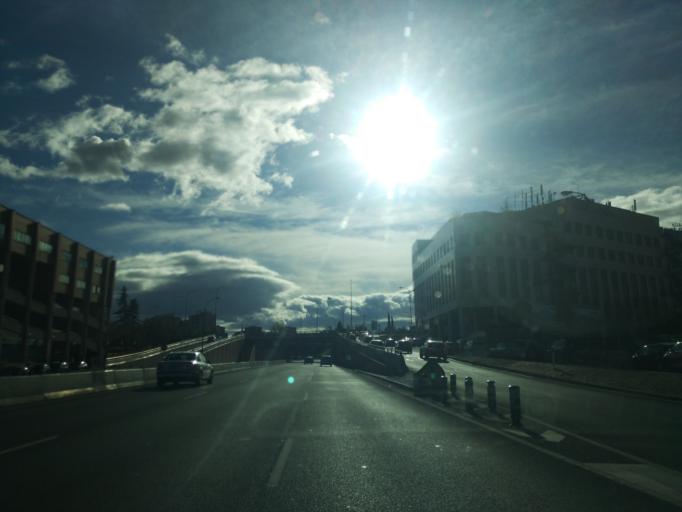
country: ES
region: Madrid
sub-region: Provincia de Madrid
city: Usera
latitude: 40.3779
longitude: -3.6935
